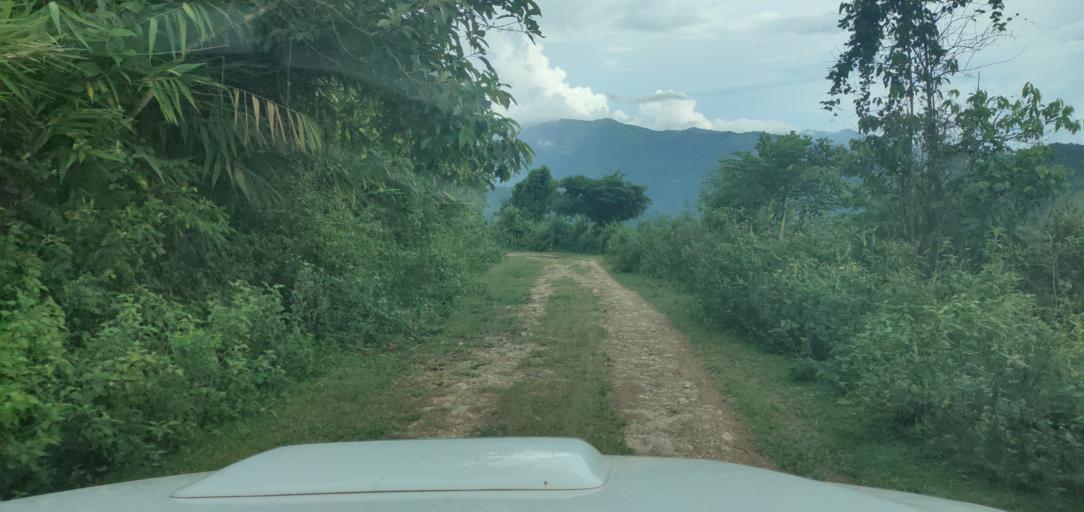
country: LA
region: Phongsali
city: Phongsali
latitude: 21.4408
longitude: 102.3243
